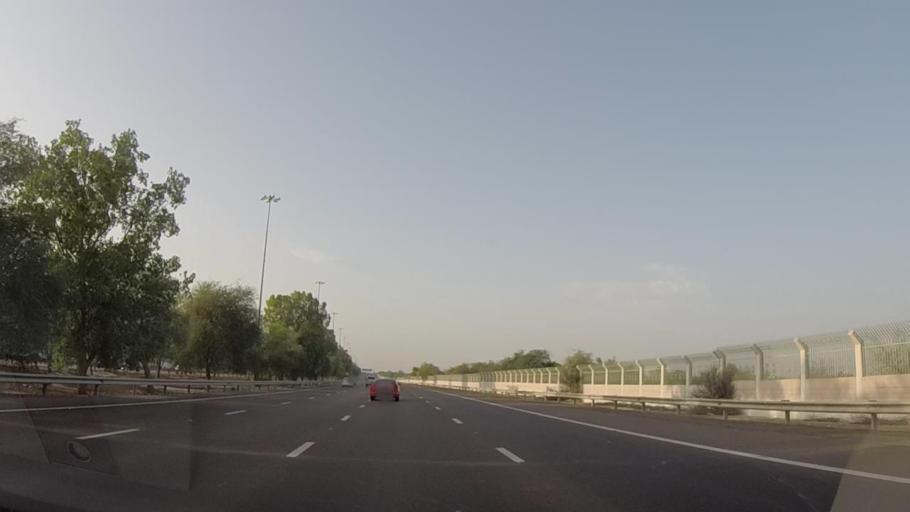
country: AE
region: Dubai
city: Dubai
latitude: 24.8130
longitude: 54.8705
